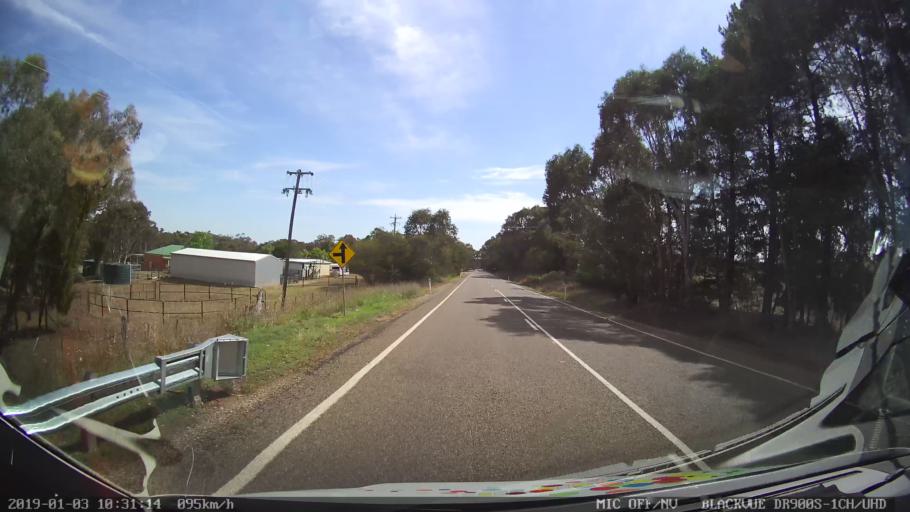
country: AU
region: New South Wales
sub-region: Young
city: Young
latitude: -34.3524
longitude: 148.2753
